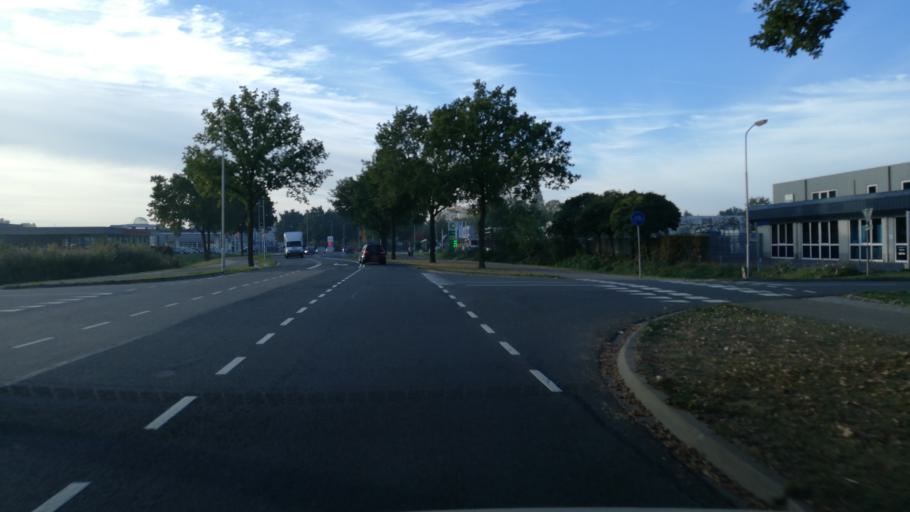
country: NL
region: Gelderland
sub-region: Gemeente Westervoort
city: Westervoort
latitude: 51.9595
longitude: 5.9829
